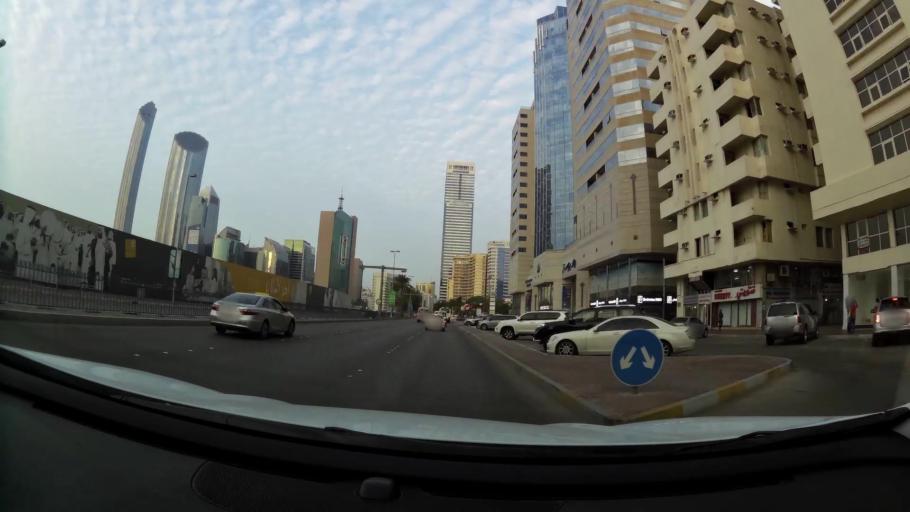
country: AE
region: Abu Dhabi
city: Abu Dhabi
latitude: 24.4801
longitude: 54.3563
